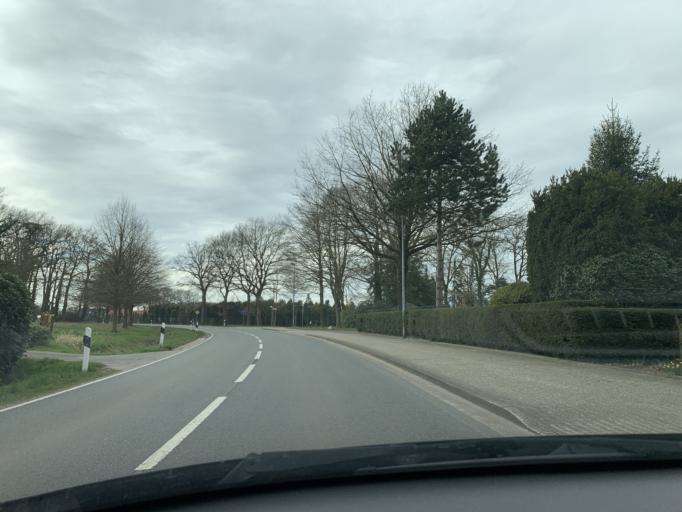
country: DE
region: Lower Saxony
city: Edewecht
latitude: 53.1579
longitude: 7.9756
